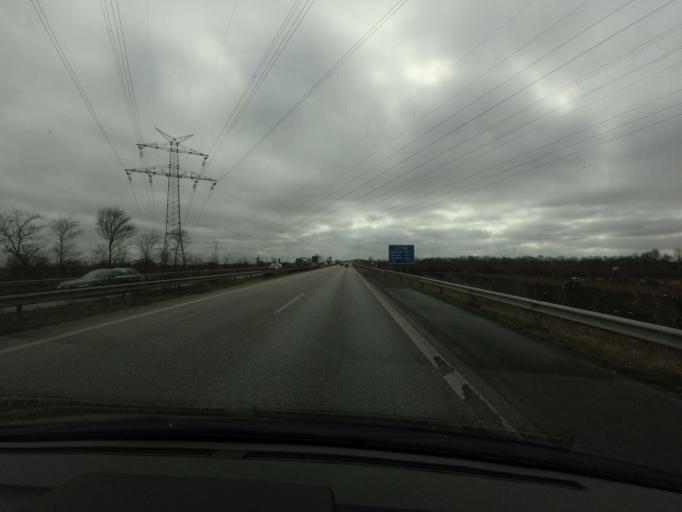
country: DE
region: Schleswig-Holstein
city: Borgstedt
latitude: 54.3424
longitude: 9.7086
